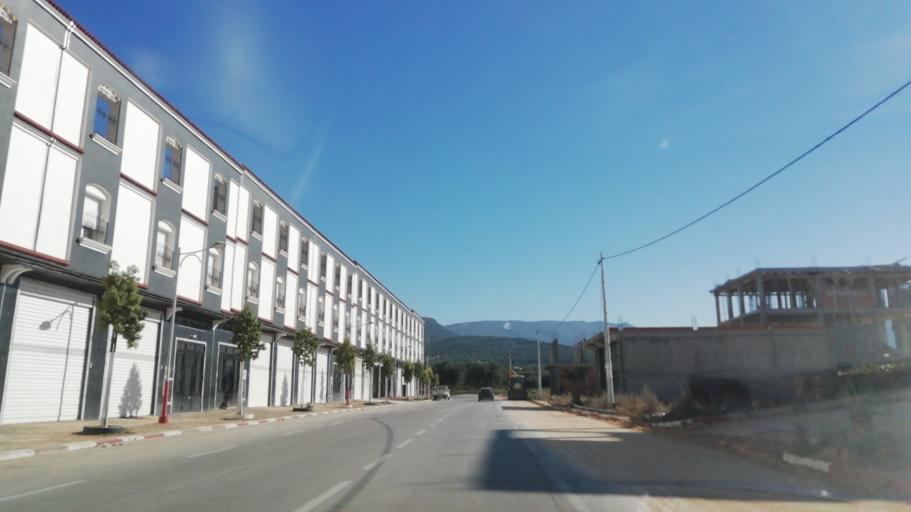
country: DZ
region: Tlemcen
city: Beni Mester
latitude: 34.8315
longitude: -1.5158
